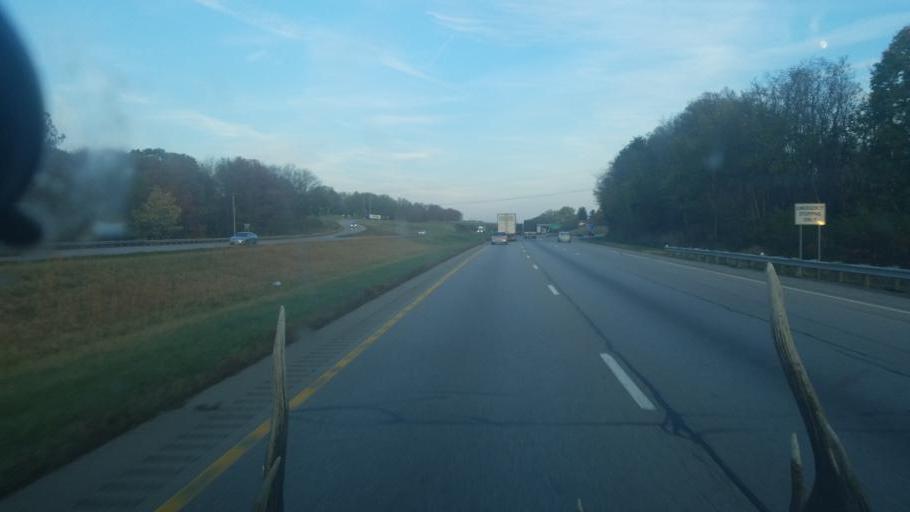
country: US
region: Ohio
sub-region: Muskingum County
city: Pleasant Grove
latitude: 39.9495
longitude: -81.9662
